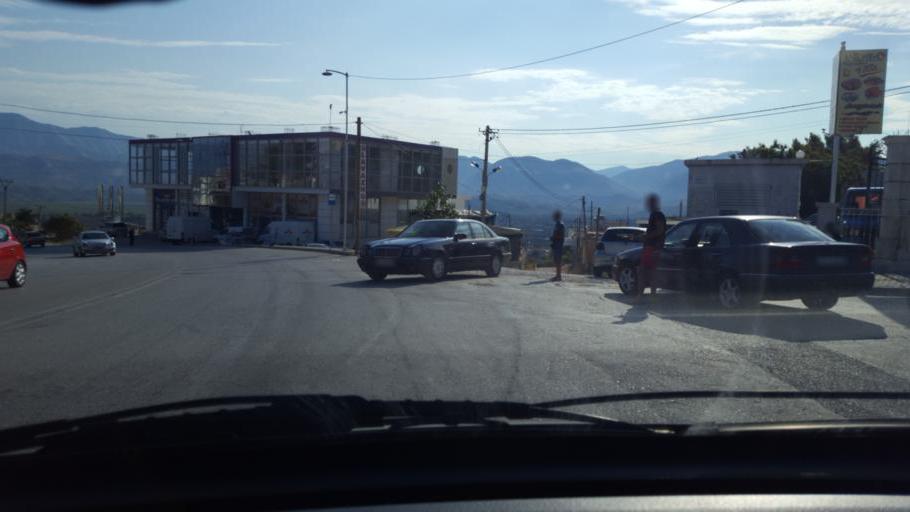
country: AL
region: Vlore
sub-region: Rrethi i Sarandes
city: Sarande
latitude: 39.8689
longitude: 20.0272
